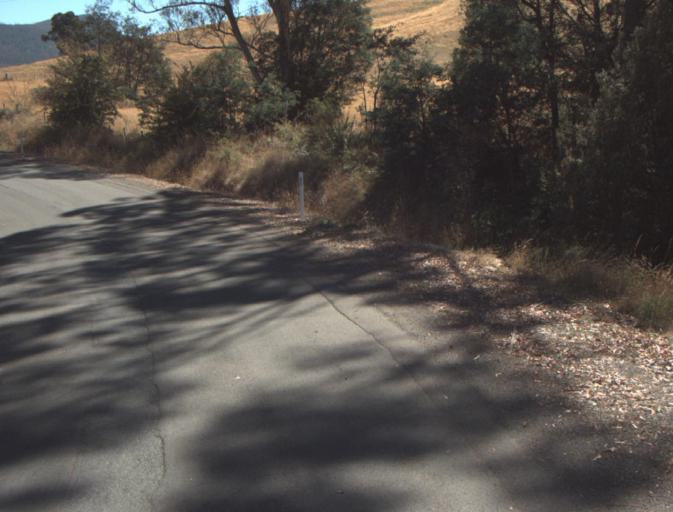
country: AU
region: Tasmania
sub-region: Launceston
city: Newstead
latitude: -41.3487
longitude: 147.3043
